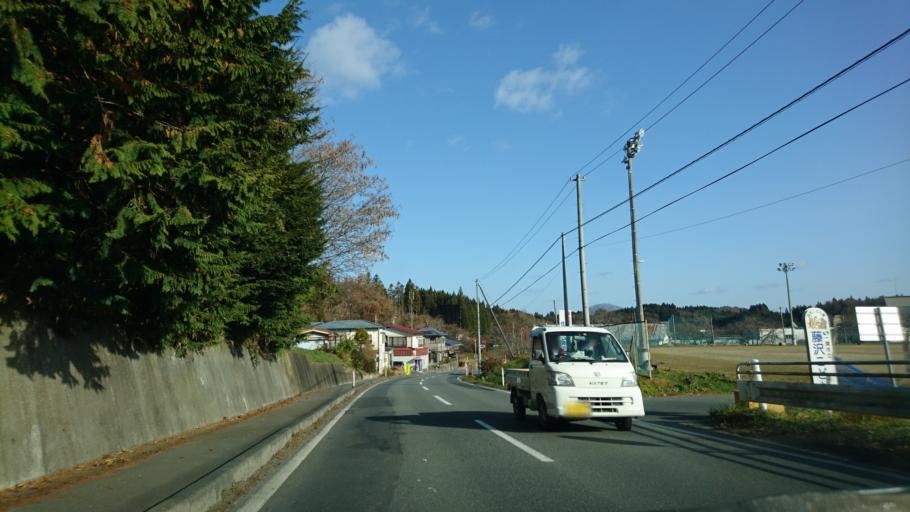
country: JP
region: Iwate
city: Ichinoseki
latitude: 38.8665
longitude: 141.3496
